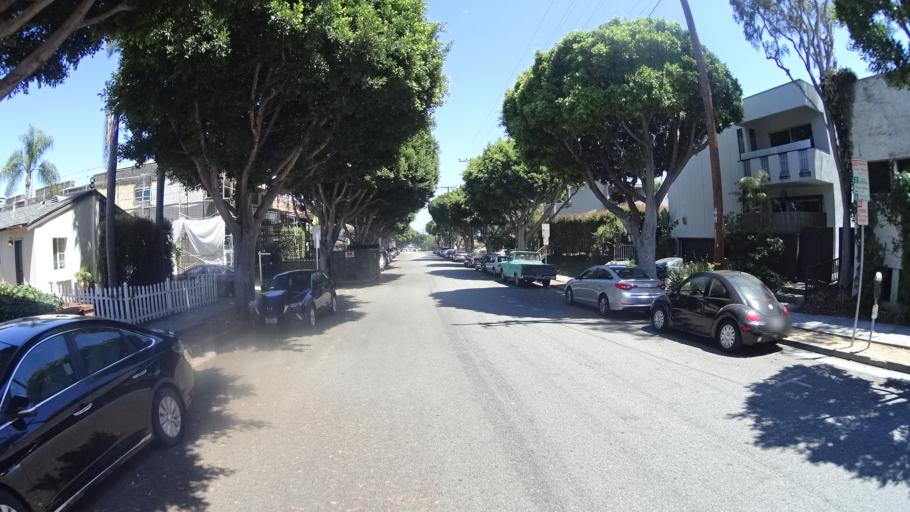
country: US
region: California
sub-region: Los Angeles County
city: Santa Monica
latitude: 34.0399
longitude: -118.4711
